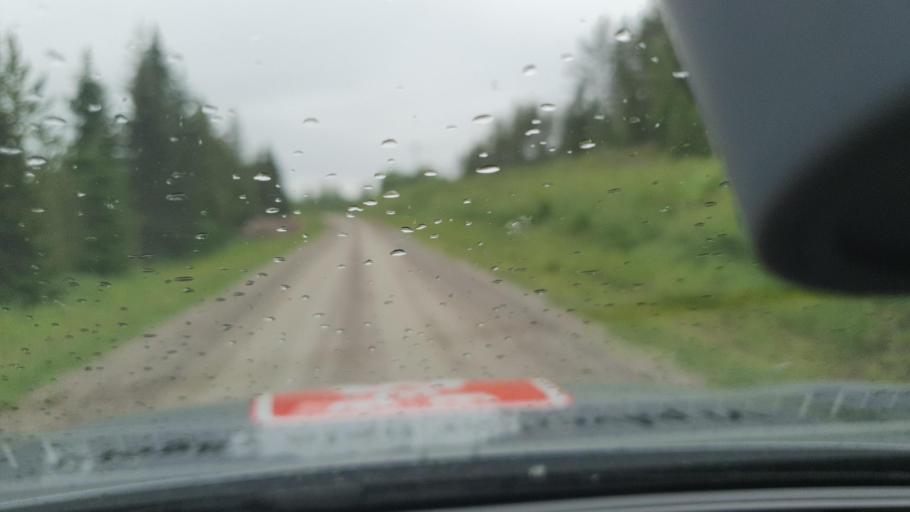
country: SE
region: Norrbotten
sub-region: Kalix Kommun
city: Rolfs
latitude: 66.0724
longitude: 22.9774
